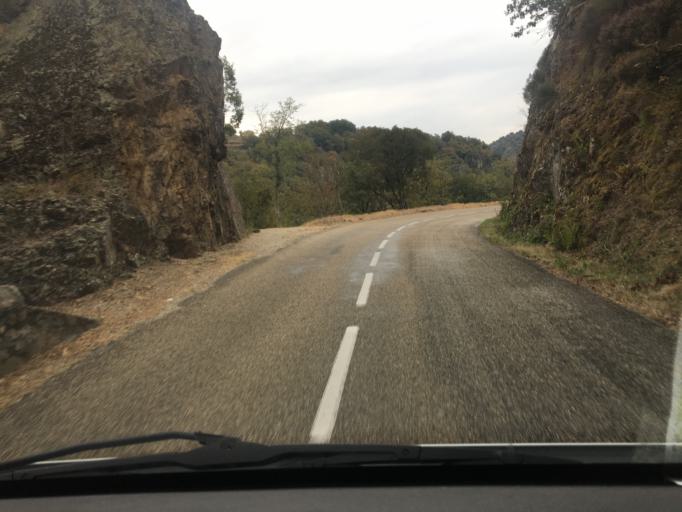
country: FR
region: Rhone-Alpes
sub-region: Departement de l'Ardeche
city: Saint-Jean-de-Muzols
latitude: 45.0587
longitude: 4.7372
